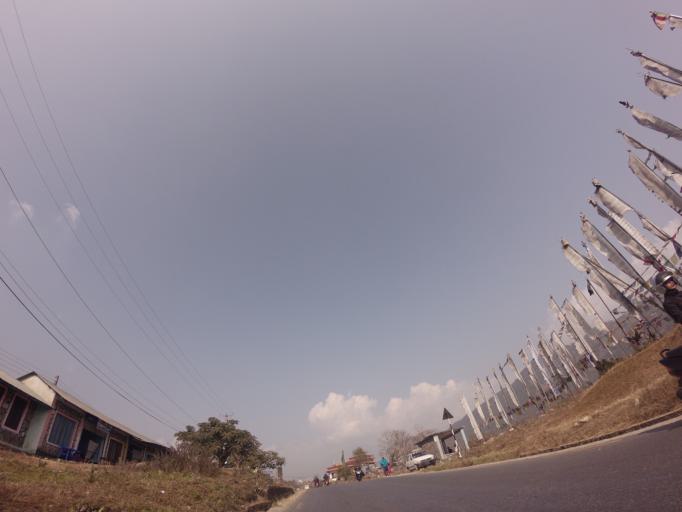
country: NP
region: Western Region
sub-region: Gandaki Zone
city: Pokhara
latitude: 28.2629
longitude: 83.9573
